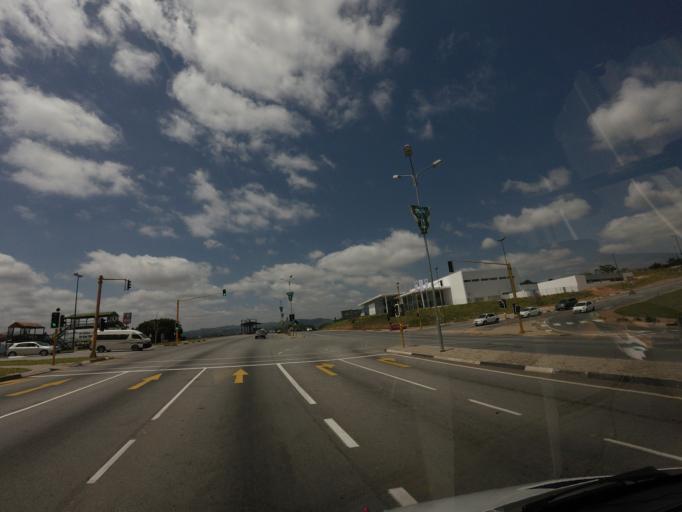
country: ZA
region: Mpumalanga
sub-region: Ehlanzeni District
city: Nelspruit
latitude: -25.4351
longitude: 30.9655
